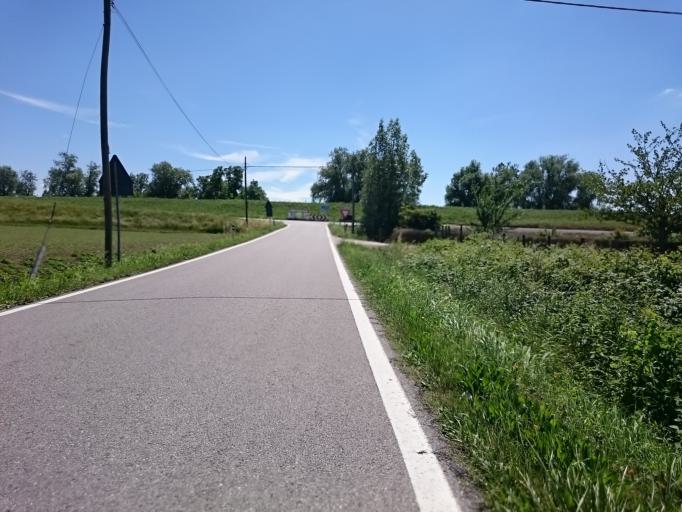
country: IT
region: Veneto
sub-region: Provincia di Padova
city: Campagnola
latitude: 45.2555
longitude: 12.0016
